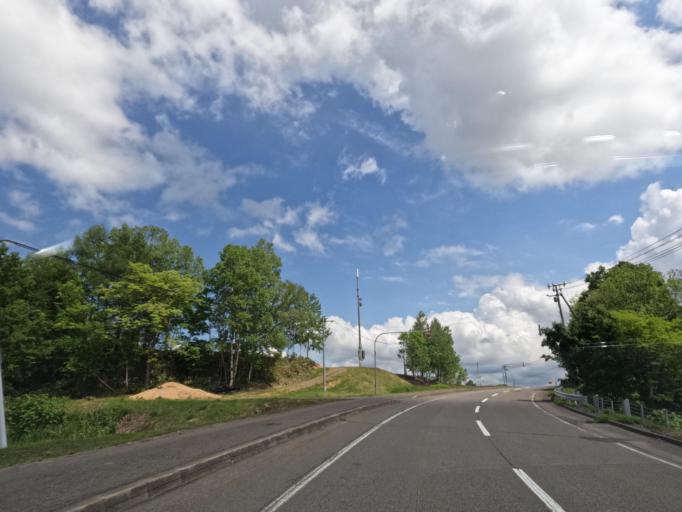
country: JP
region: Hokkaido
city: Takikawa
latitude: 43.5819
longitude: 141.8189
